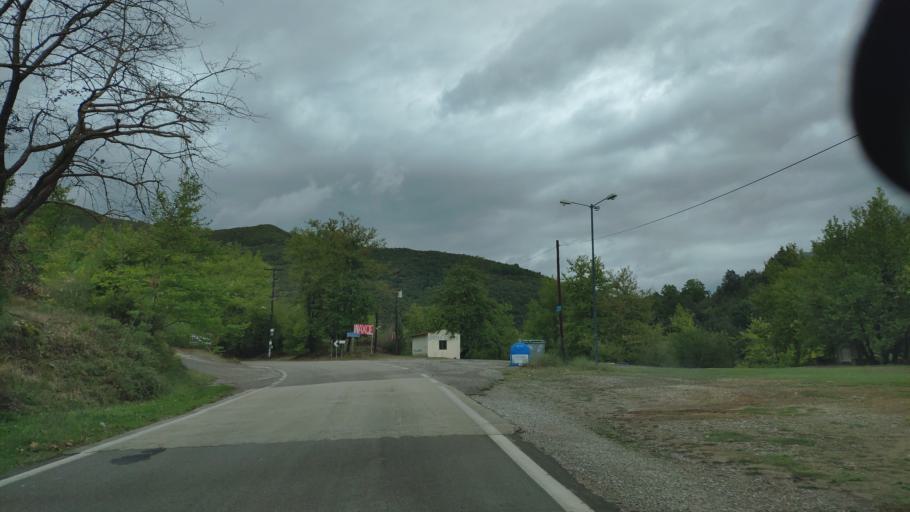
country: GR
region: West Greece
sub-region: Nomos Aitolias kai Akarnanias
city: Sardinia
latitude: 38.9433
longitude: 21.3419
